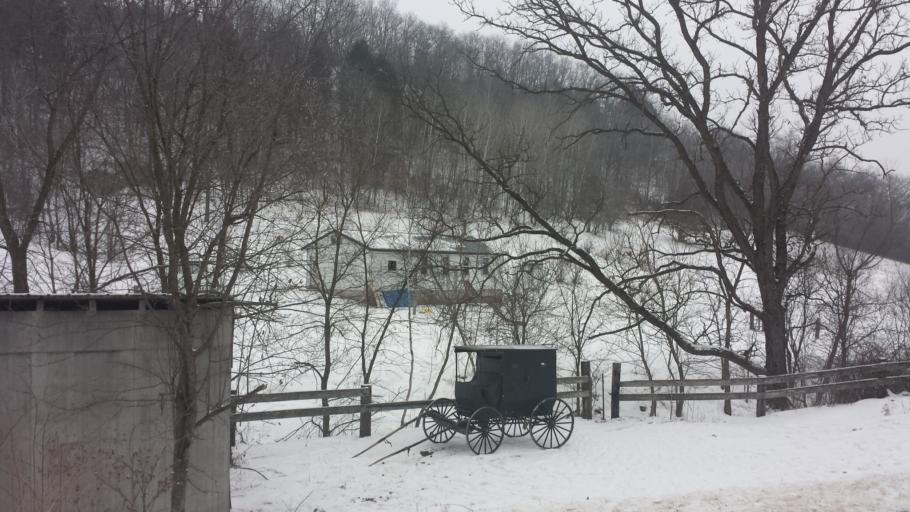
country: US
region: Wisconsin
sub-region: Monroe County
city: Cashton
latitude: 43.7570
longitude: -90.6835
